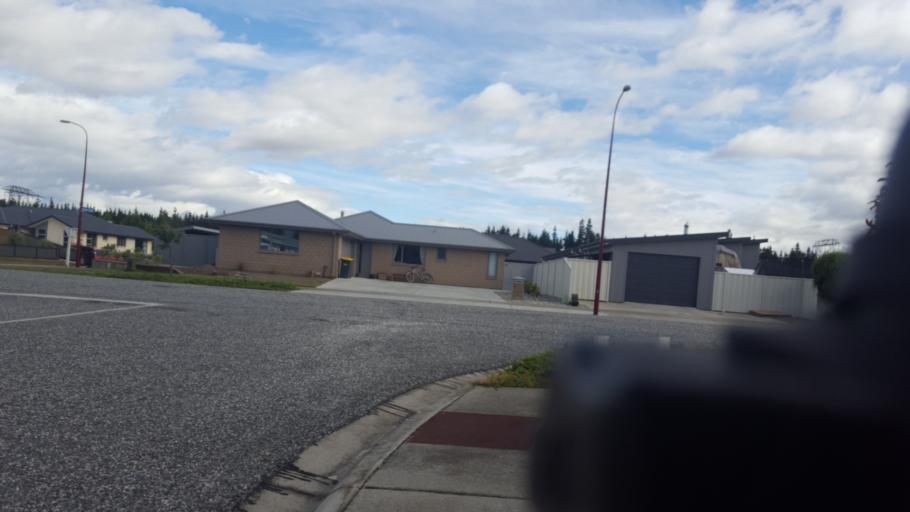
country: NZ
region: Otago
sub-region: Queenstown-Lakes District
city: Wanaka
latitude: -45.2391
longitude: 169.3816
